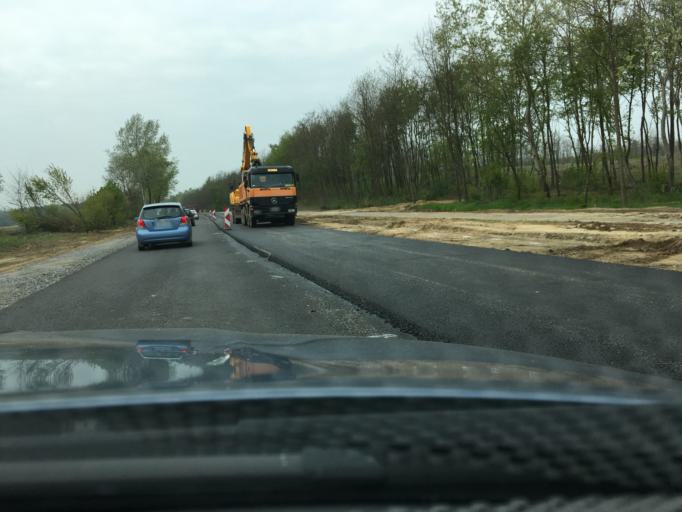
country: HU
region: Hajdu-Bihar
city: Nyiradony
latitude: 47.6789
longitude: 21.8730
